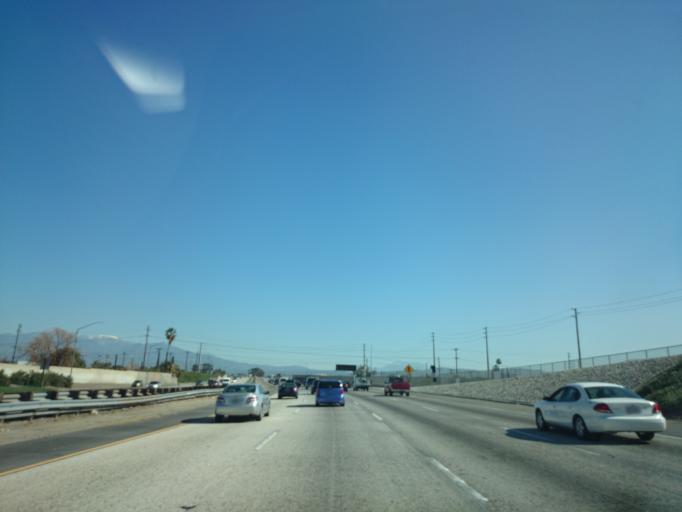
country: US
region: California
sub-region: San Bernardino County
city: Colton
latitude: 34.0671
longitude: -117.3350
